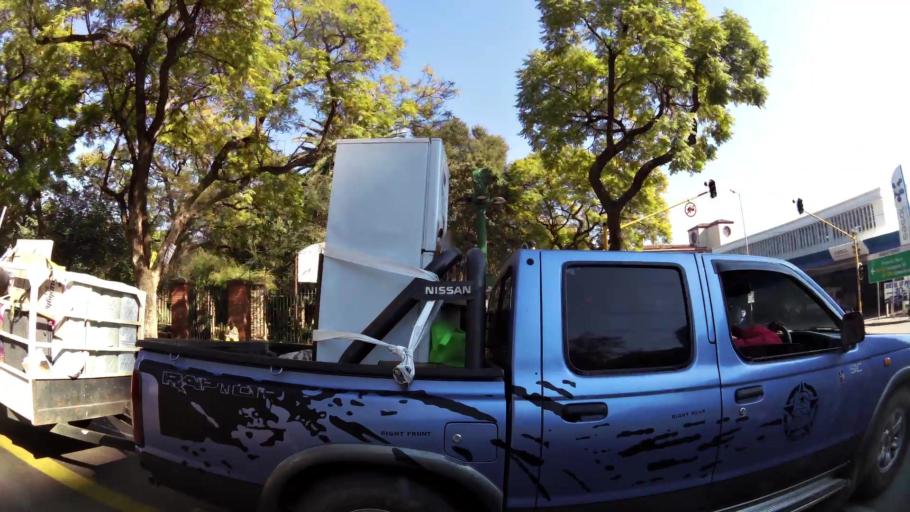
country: ZA
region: Gauteng
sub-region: City of Tshwane Metropolitan Municipality
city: Pretoria
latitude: -25.7526
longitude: 28.1861
